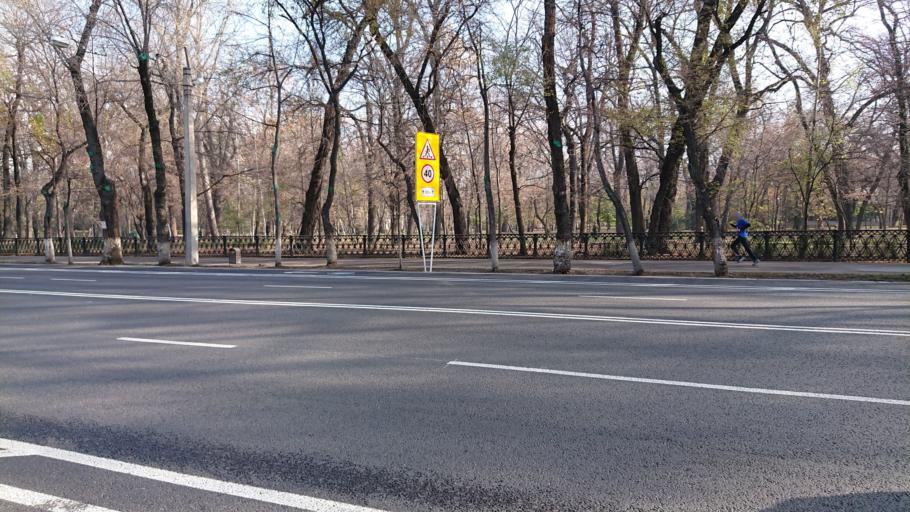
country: KZ
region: Almaty Qalasy
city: Almaty
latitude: 43.2577
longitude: 76.9498
